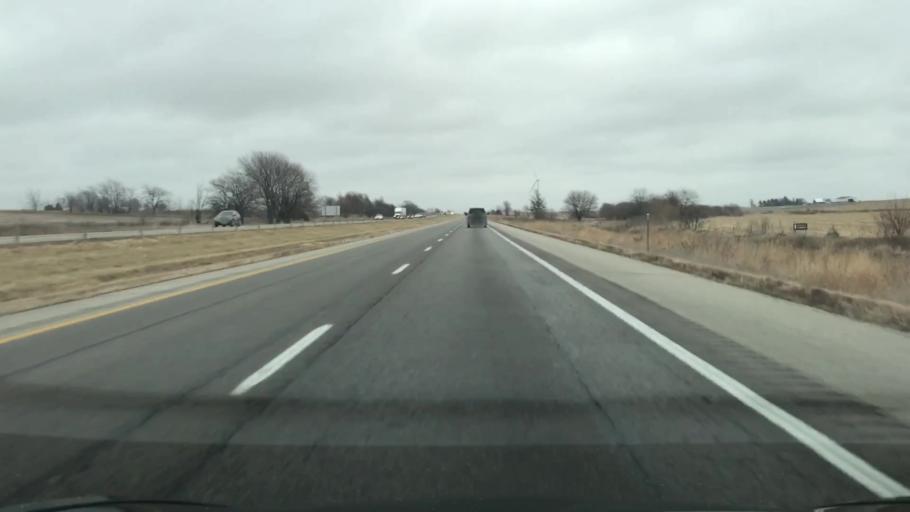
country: US
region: Iowa
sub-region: Guthrie County
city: Stuart
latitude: 41.4929
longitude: -94.2834
